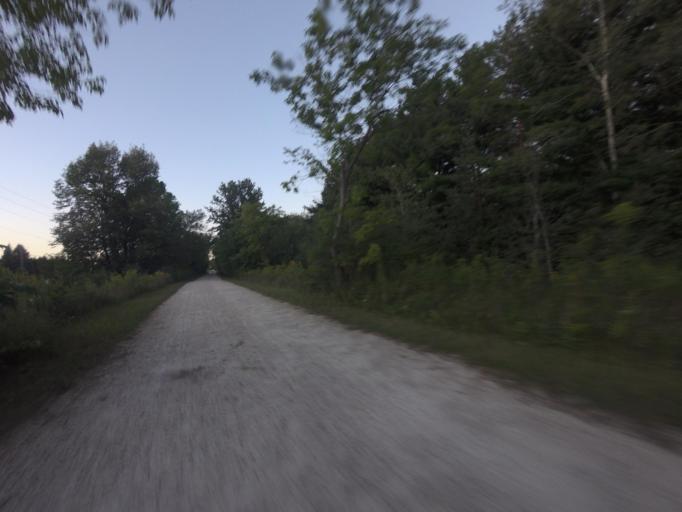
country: CA
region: Ontario
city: Orangeville
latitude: 43.9535
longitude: -79.8341
